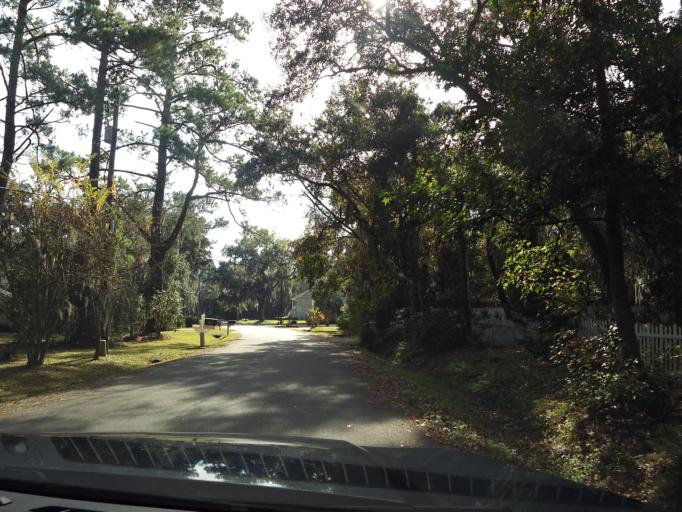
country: US
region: Georgia
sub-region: Glynn County
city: Brunswick
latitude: 31.1247
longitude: -81.5533
